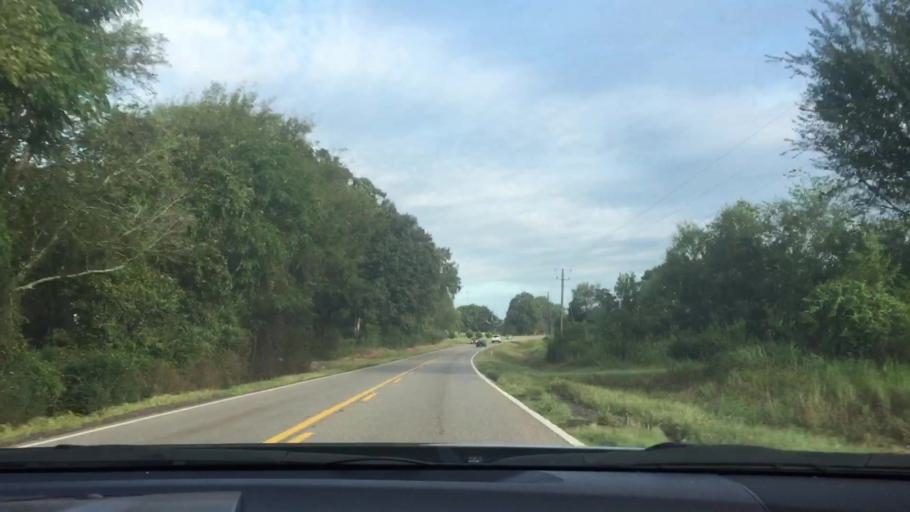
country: US
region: Alabama
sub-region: Hale County
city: Moundville
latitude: 32.9053
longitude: -87.6344
